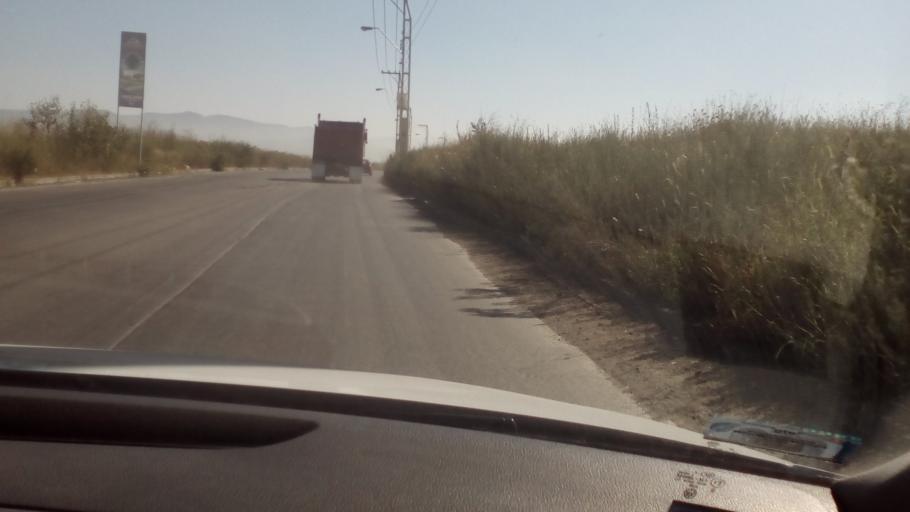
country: MX
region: Guanajuato
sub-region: Leon
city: Fraccionamiento Paseo de las Torres
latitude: 21.1716
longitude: -101.7522
